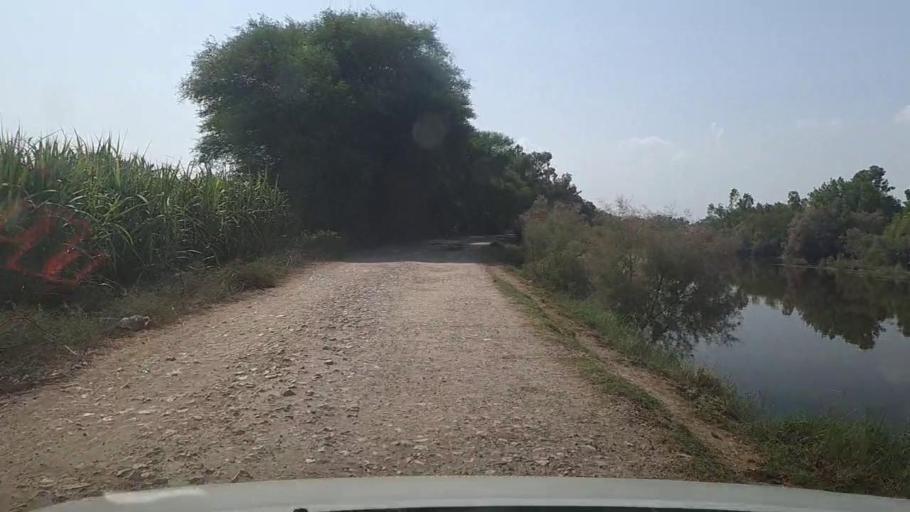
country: PK
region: Sindh
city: Khairpur
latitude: 28.1214
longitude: 69.6076
